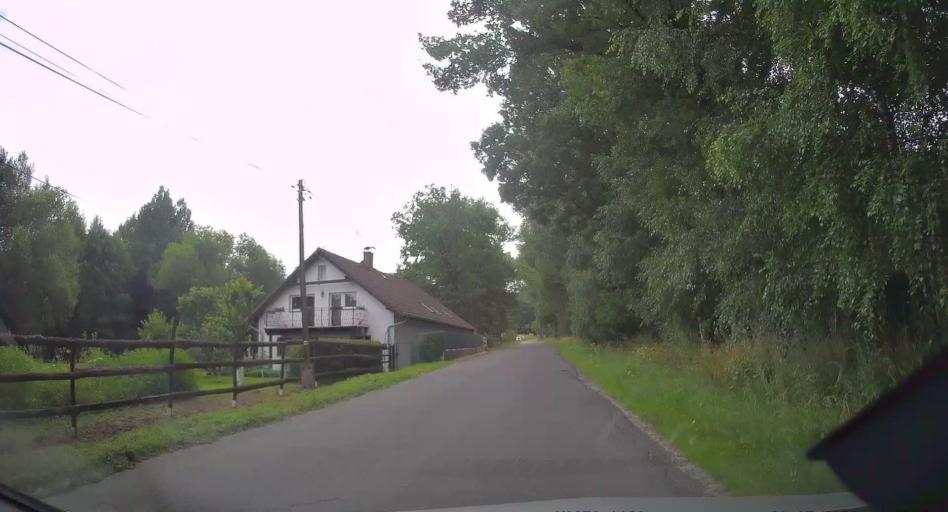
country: PL
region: Lower Silesian Voivodeship
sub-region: Powiat kamiennogorski
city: Marciszow
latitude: 50.8391
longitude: 15.9782
